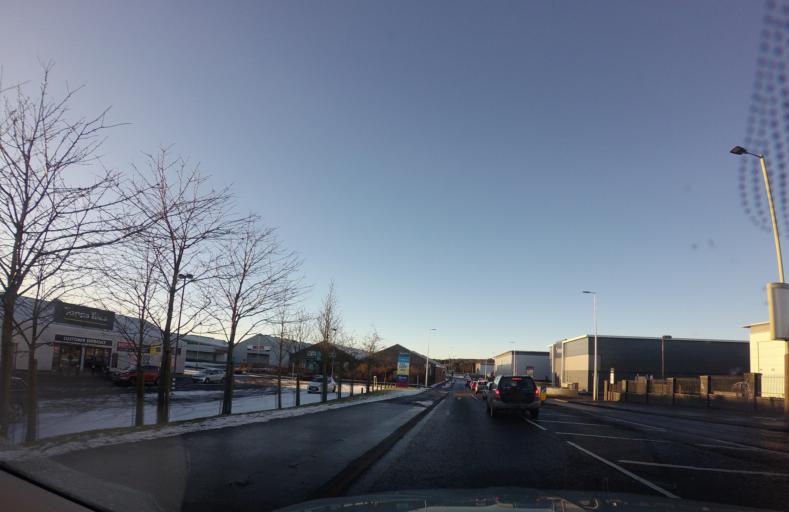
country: GB
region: Scotland
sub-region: Dundee City
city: Dundee
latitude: 56.4803
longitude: -2.9957
